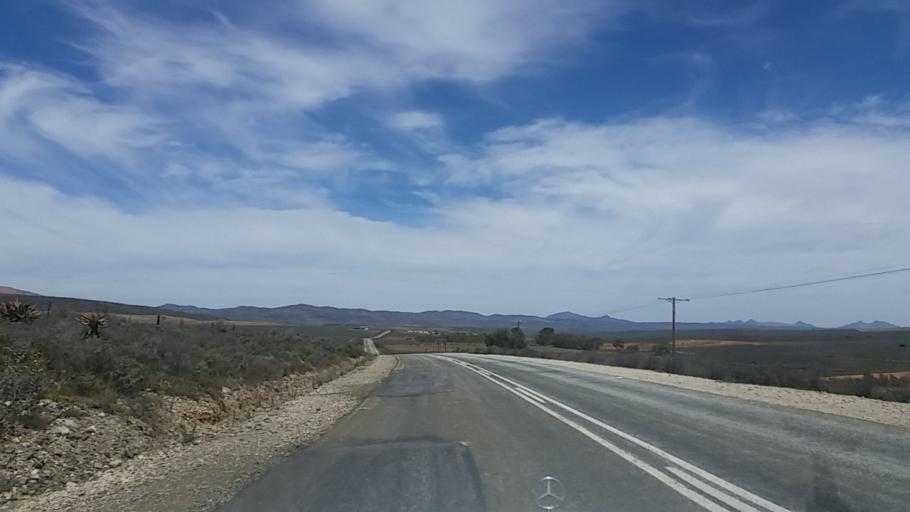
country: ZA
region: Eastern Cape
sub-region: Cacadu District Municipality
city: Willowmore
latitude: -33.5919
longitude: 23.1526
